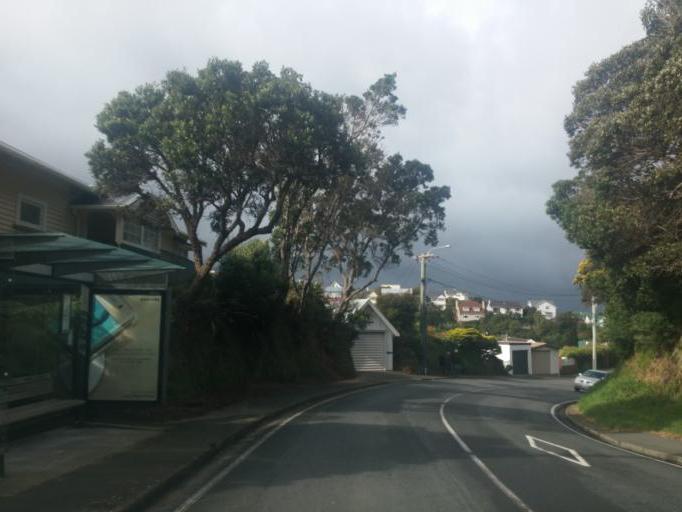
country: NZ
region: Wellington
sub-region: Wellington City
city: Kelburn
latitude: -41.2625
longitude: 174.7770
